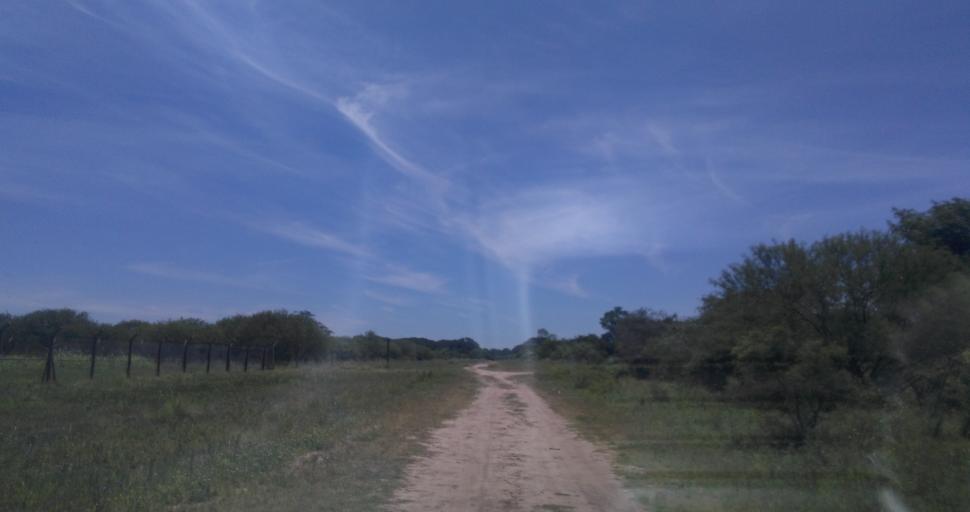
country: AR
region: Chaco
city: Fontana
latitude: -27.4294
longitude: -59.0489
